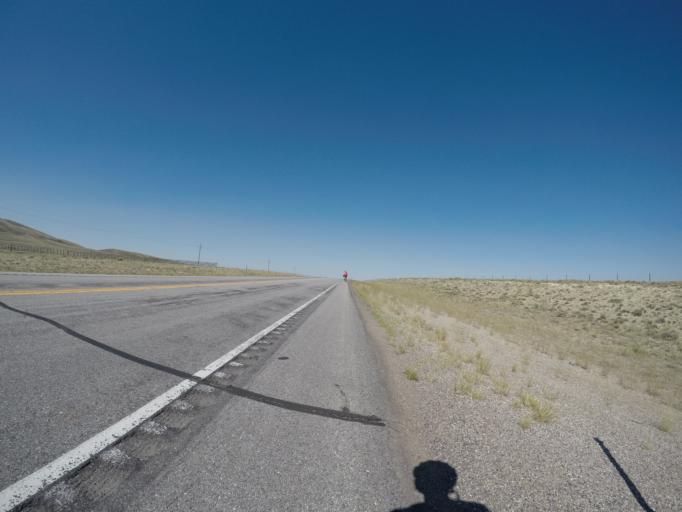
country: US
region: Wyoming
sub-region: Carbon County
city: Saratoga
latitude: 41.7953
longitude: -106.7293
